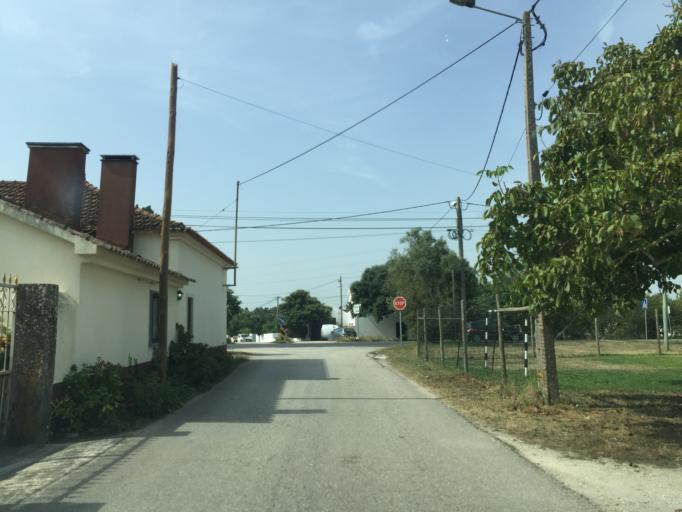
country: PT
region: Leiria
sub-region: Alcobaca
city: Benedita
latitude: 39.4078
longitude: -8.9645
